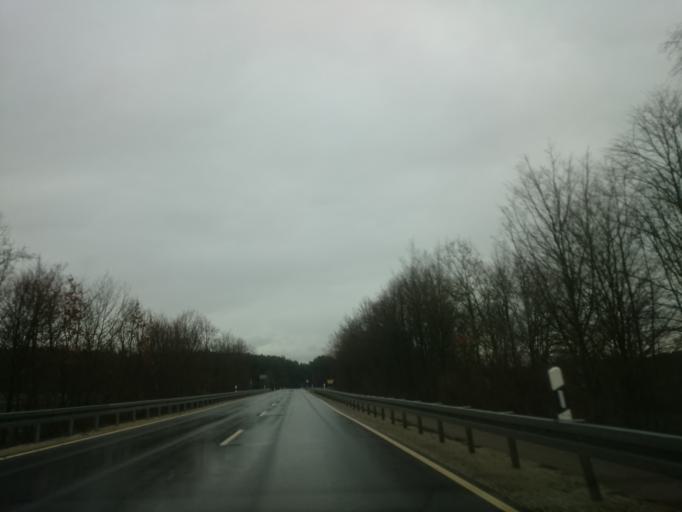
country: DE
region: Bavaria
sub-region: Regierungsbezirk Mittelfranken
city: Hilpoltstein
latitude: 49.1991
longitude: 11.2077
